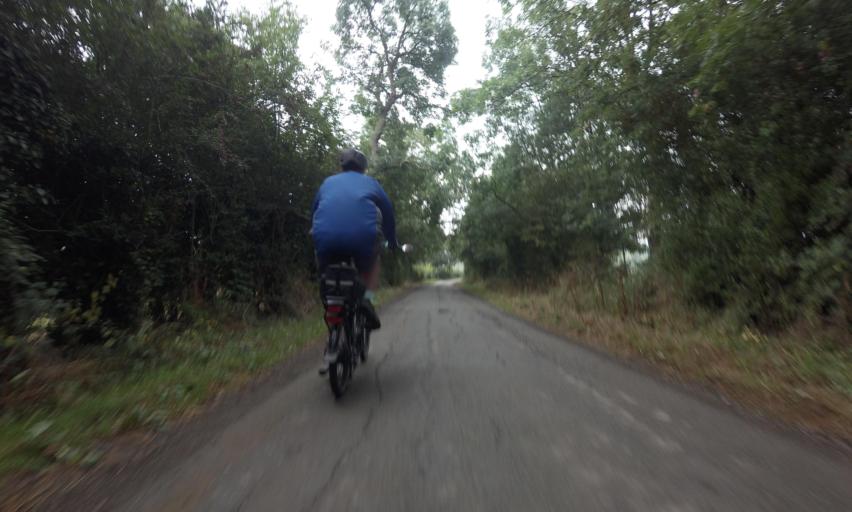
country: GB
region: England
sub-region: Gloucestershire
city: Gotherington
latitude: 51.9839
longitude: -2.0263
